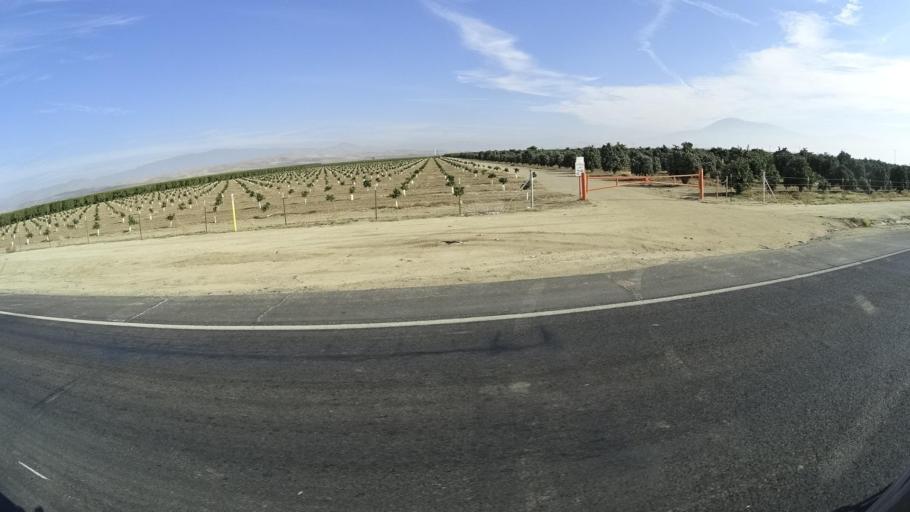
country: US
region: California
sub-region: Kern County
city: Lamont
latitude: 35.3440
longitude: -118.8432
